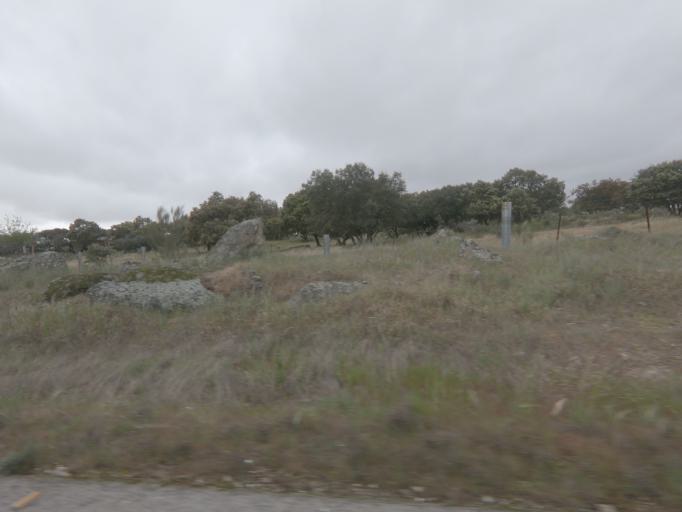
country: ES
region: Extremadura
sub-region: Provincia de Caceres
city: Caceres
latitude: 39.3995
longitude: -6.4220
